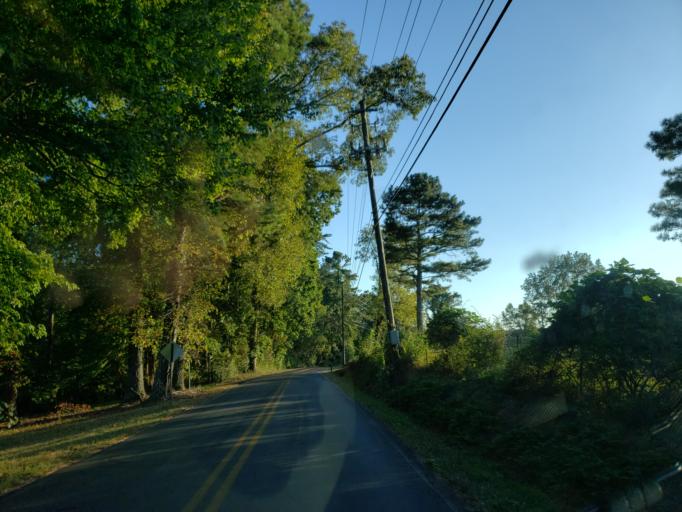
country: US
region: Georgia
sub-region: Pickens County
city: Jasper
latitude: 34.4617
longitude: -84.4327
